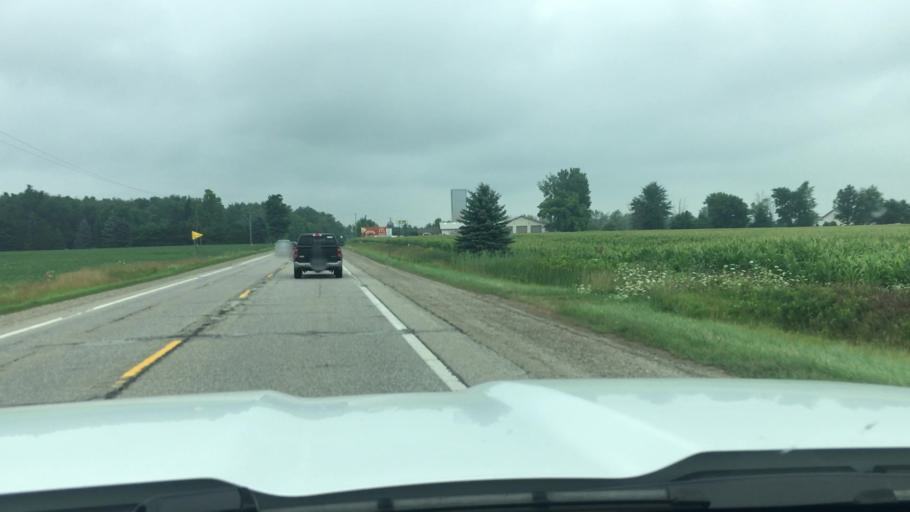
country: US
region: Michigan
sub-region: Sanilac County
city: Marlette
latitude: 43.2450
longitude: -83.0788
